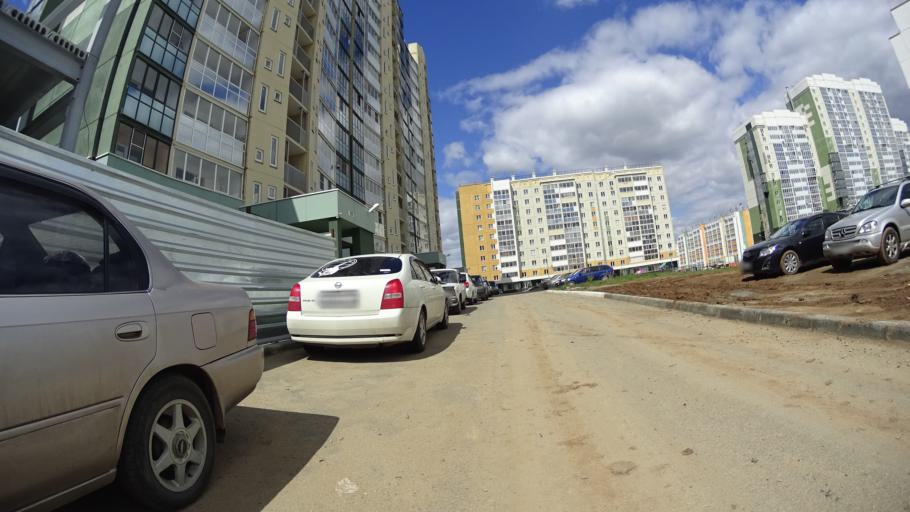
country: RU
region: Chelyabinsk
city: Roshchino
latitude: 55.1714
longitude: 61.2562
